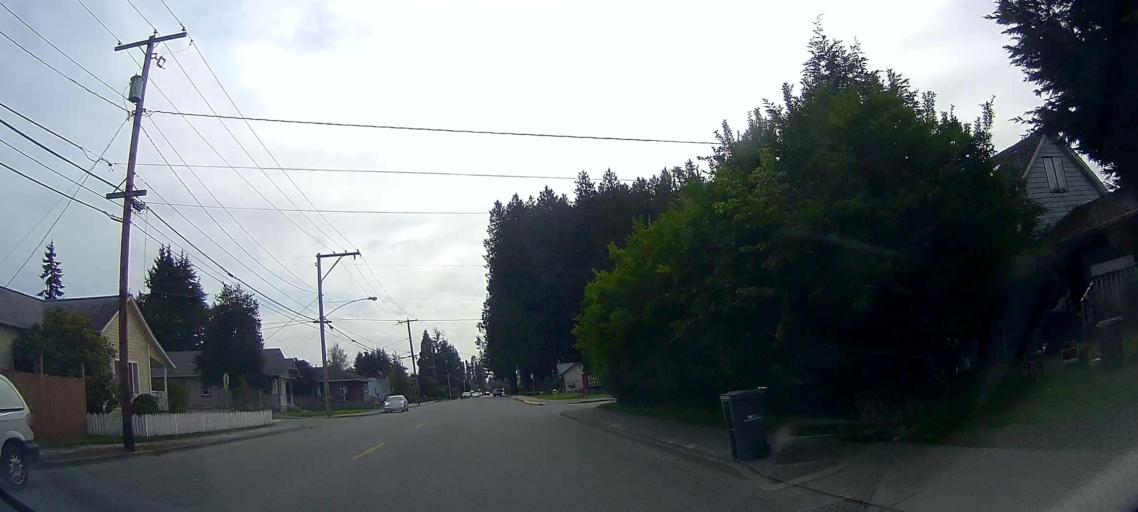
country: US
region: Washington
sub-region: Skagit County
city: Burlington
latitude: 48.4750
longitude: -122.3192
